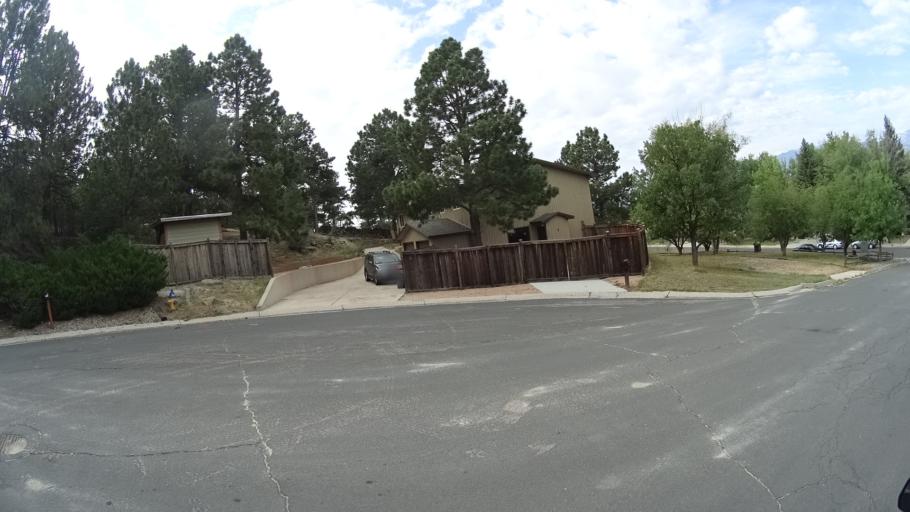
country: US
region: Colorado
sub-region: El Paso County
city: Cimarron Hills
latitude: 38.8679
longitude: -104.7521
